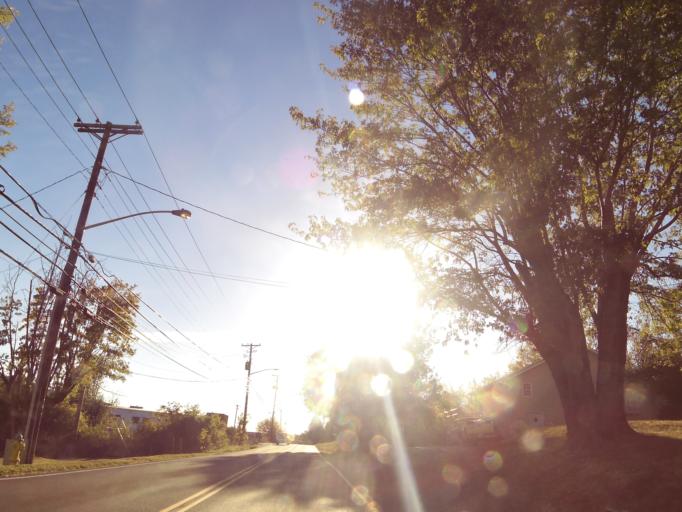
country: US
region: Tennessee
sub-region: Knox County
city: Knoxville
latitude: 36.0098
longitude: -83.9446
